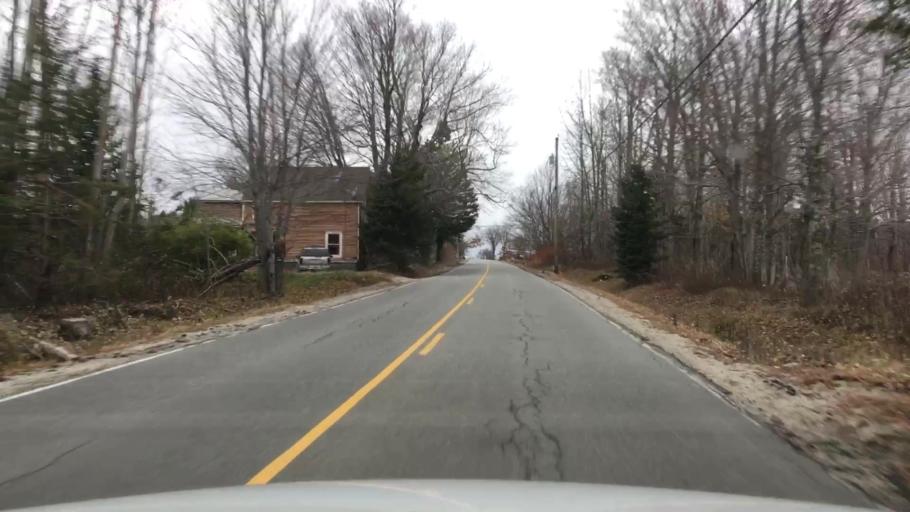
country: US
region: Maine
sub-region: Hancock County
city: Penobscot
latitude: 44.4355
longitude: -68.6318
